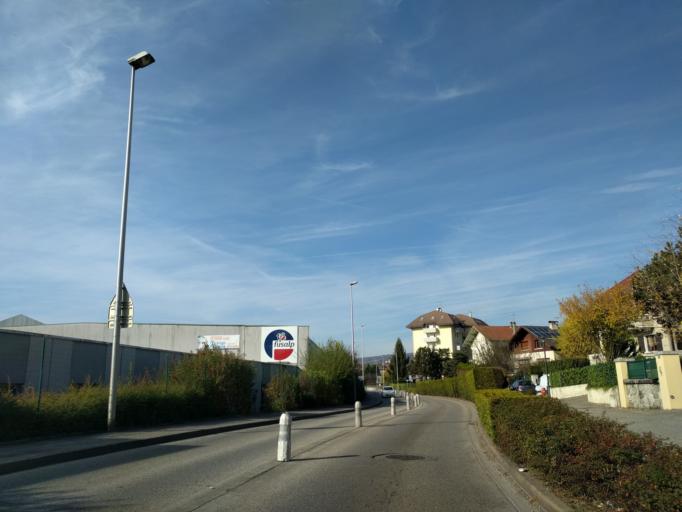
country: FR
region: Rhone-Alpes
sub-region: Departement de la Haute-Savoie
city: Annecy-le-Vieux
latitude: 45.9230
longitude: 6.1309
